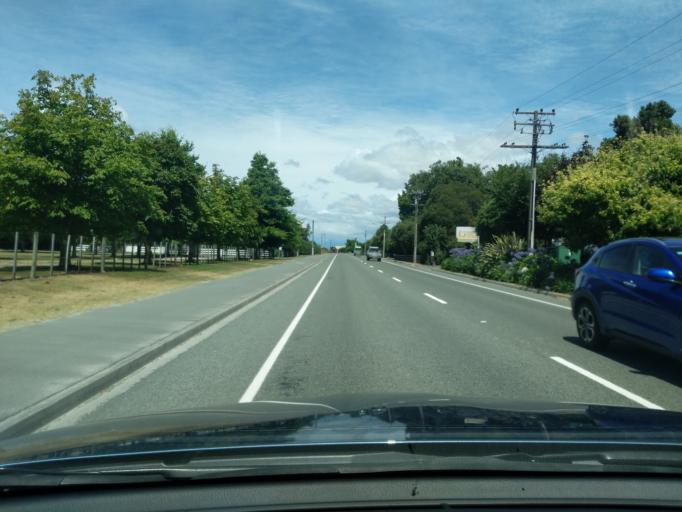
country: NZ
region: Tasman
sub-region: Tasman District
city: Motueka
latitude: -41.0952
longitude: 173.0119
